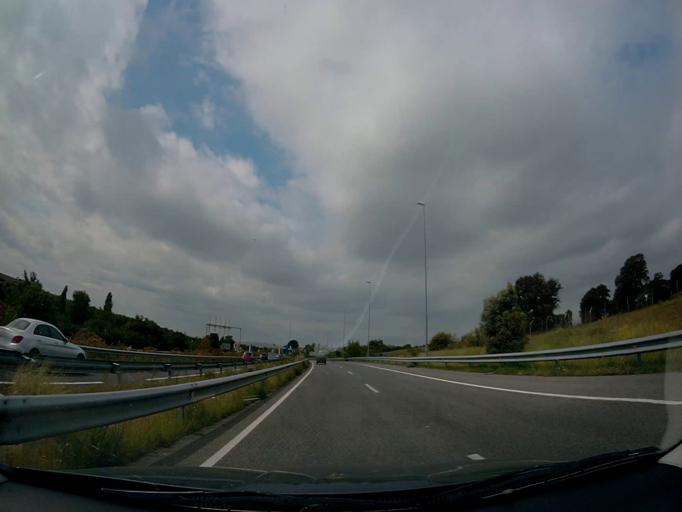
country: ES
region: Madrid
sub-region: Provincia de Madrid
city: Boadilla del Monte
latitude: 40.3936
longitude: -3.8941
